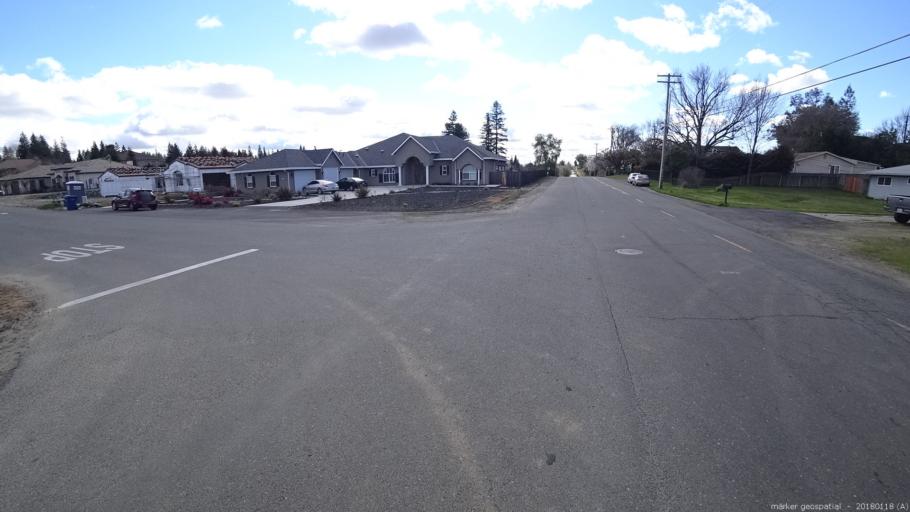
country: US
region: California
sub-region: Sacramento County
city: Folsom
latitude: 38.6970
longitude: -121.1947
